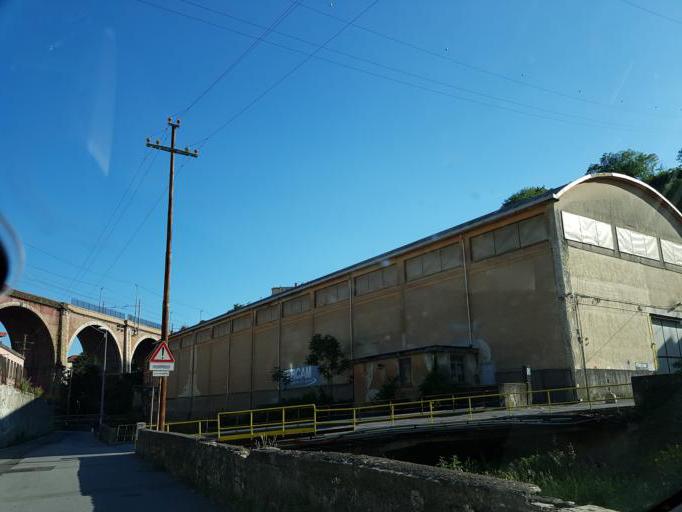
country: IT
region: Liguria
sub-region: Provincia di Genova
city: Genoa
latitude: 44.4545
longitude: 8.8897
